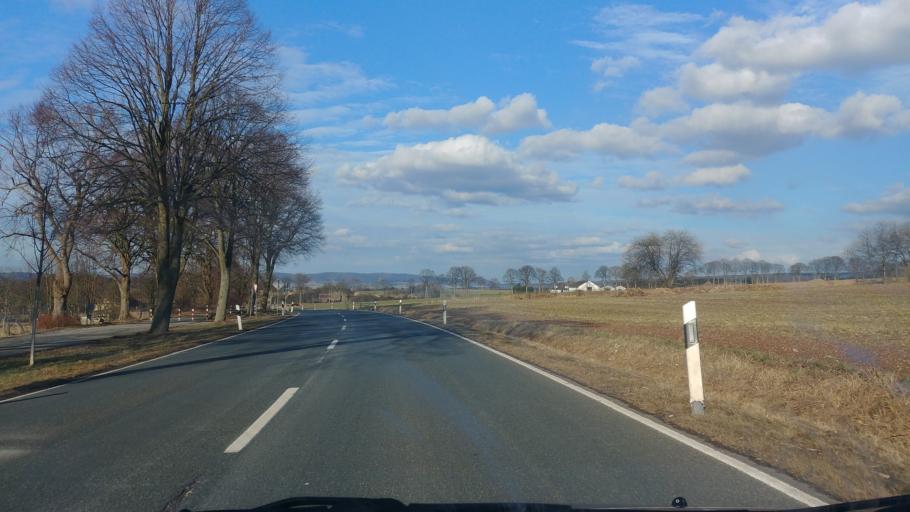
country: DE
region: Lower Saxony
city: Holzminden
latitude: 51.7942
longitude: 9.4492
